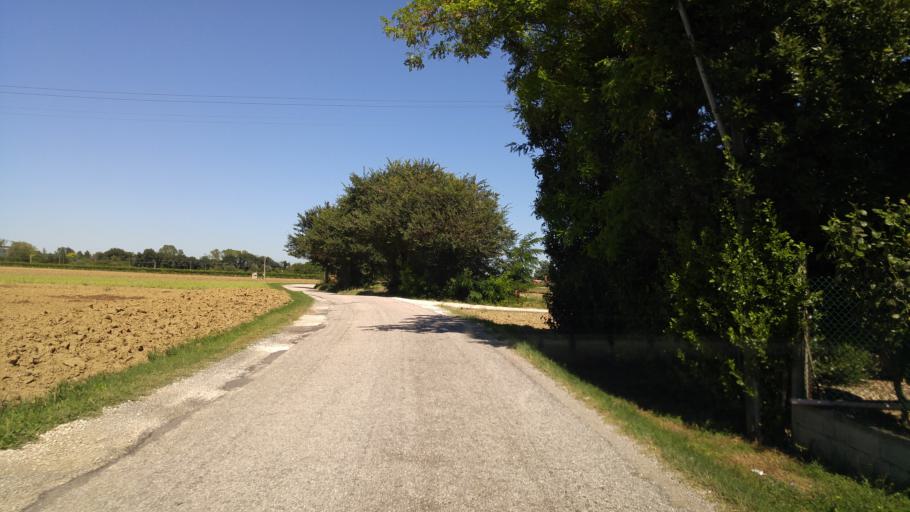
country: IT
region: The Marches
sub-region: Provincia di Pesaro e Urbino
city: Lucrezia
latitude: 43.7729
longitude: 12.9572
